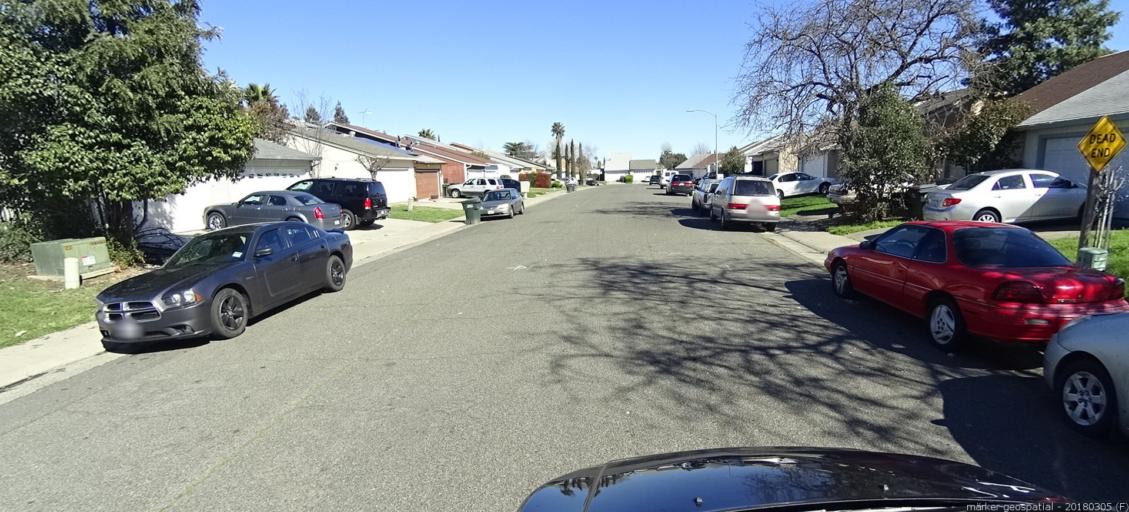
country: US
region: California
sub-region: Sacramento County
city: Florin
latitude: 38.4835
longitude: -121.4199
